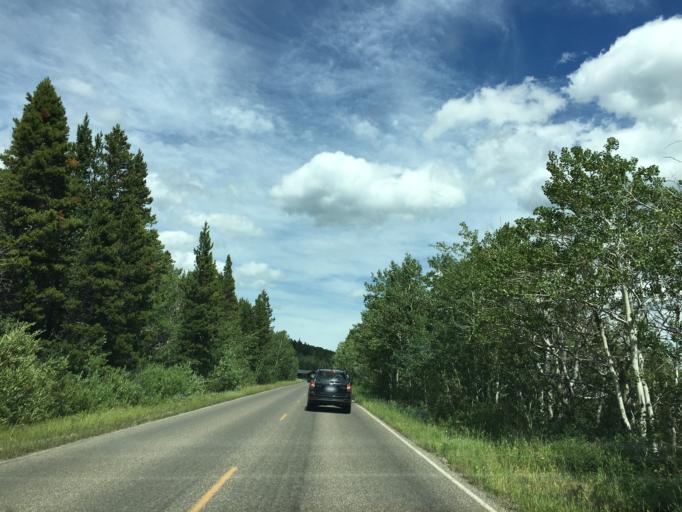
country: CA
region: Alberta
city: Cardston
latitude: 48.8208
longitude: -113.5827
